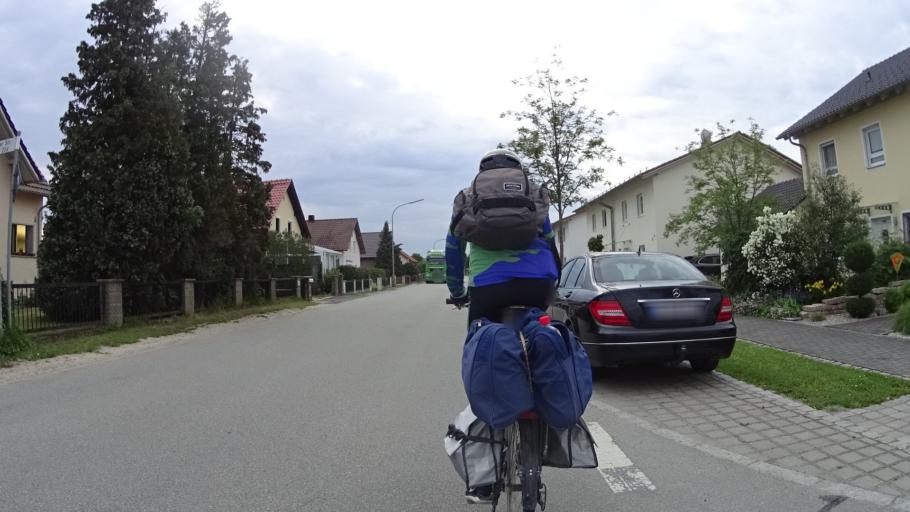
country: DE
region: Bavaria
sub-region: Lower Bavaria
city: Parkstetten
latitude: 48.9183
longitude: 12.5898
